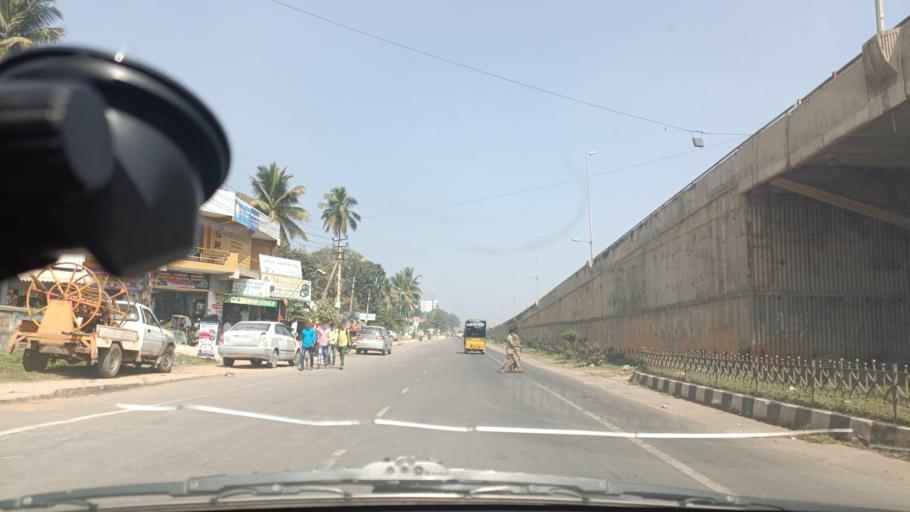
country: IN
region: Karnataka
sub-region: Bangalore Urban
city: Yelahanka
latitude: 13.1065
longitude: 77.6016
